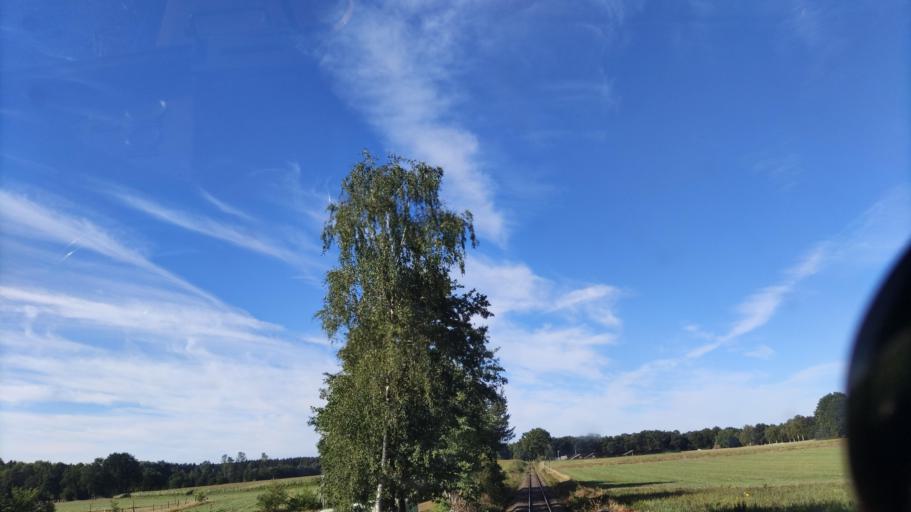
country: DE
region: Lower Saxony
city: Soderstorf
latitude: 53.1291
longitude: 10.1311
